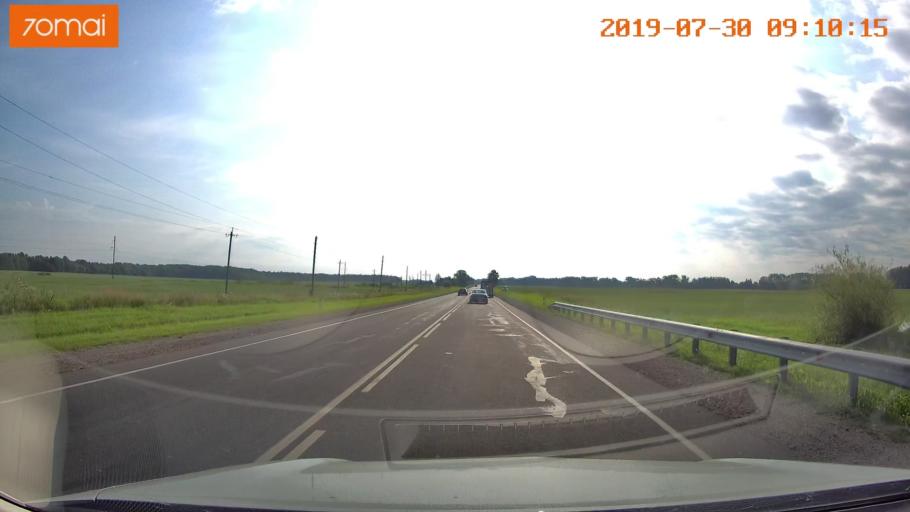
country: RU
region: Kaliningrad
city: Nesterov
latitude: 54.6121
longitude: 22.4229
